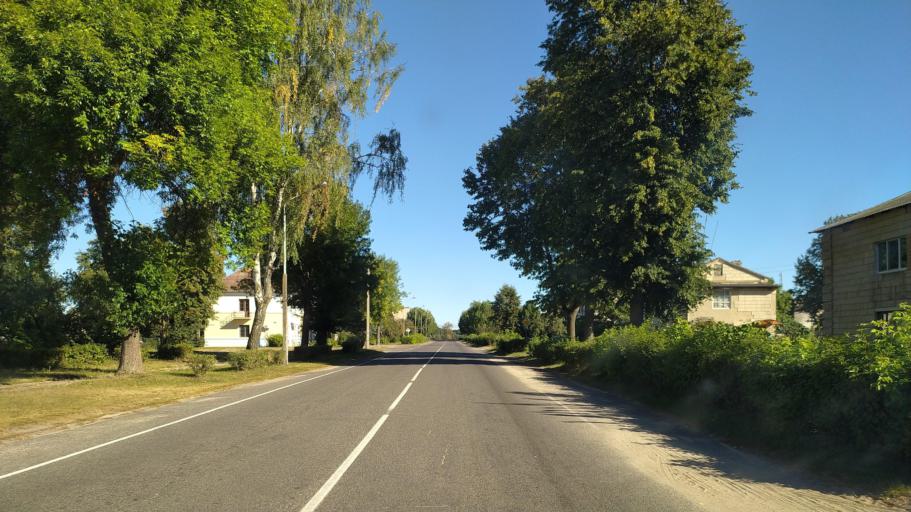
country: BY
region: Brest
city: Pruzhany
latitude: 52.4891
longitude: 24.7078
